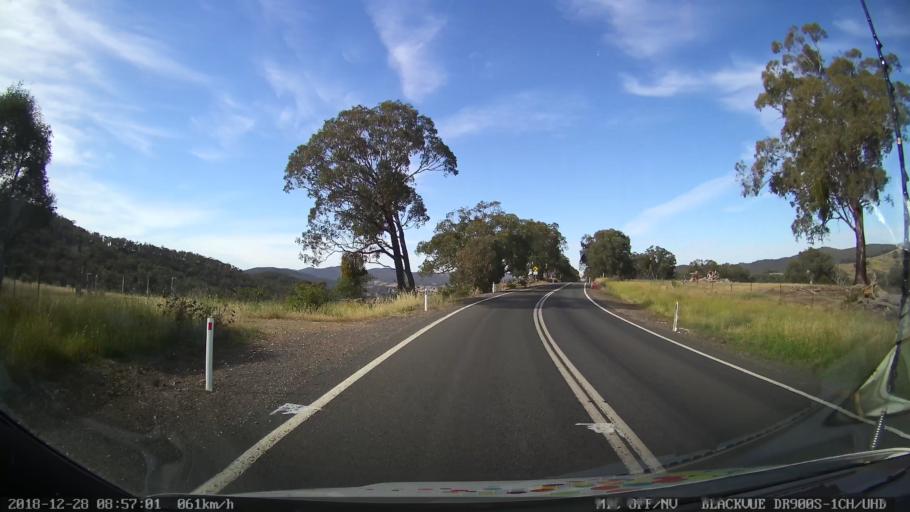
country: AU
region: New South Wales
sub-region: Upper Lachlan Shire
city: Crookwell
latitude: -34.1158
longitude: 149.3379
